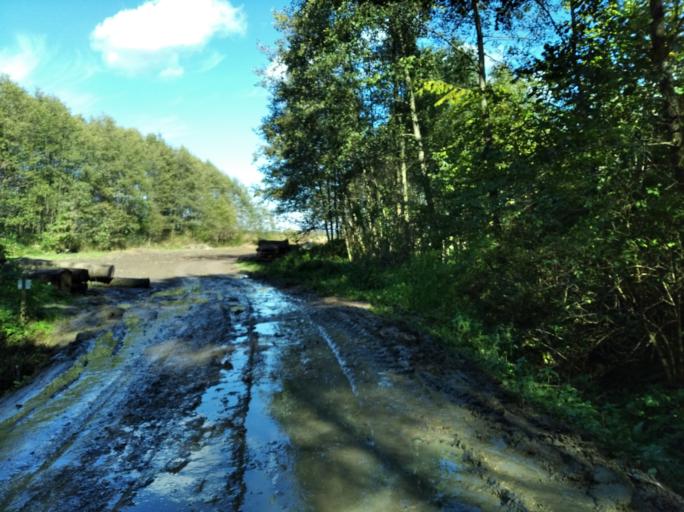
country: PL
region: Subcarpathian Voivodeship
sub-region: Powiat strzyzowski
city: Strzyzow
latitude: 49.8347
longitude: 21.7983
